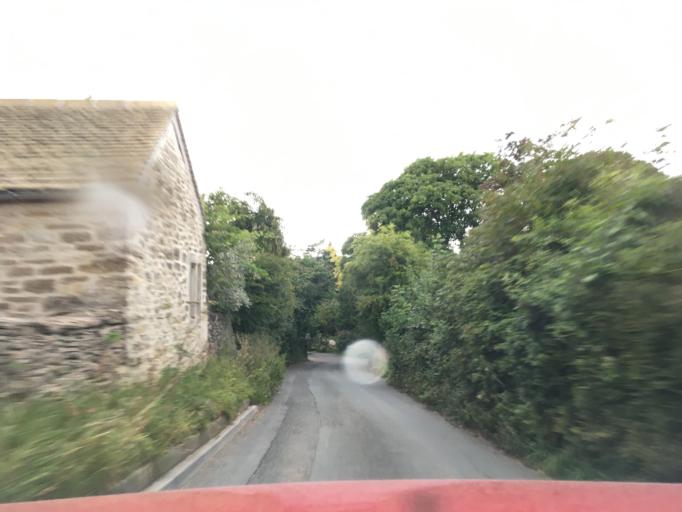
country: GB
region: England
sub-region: Gloucestershire
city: Shurdington
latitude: 51.8135
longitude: -2.1458
